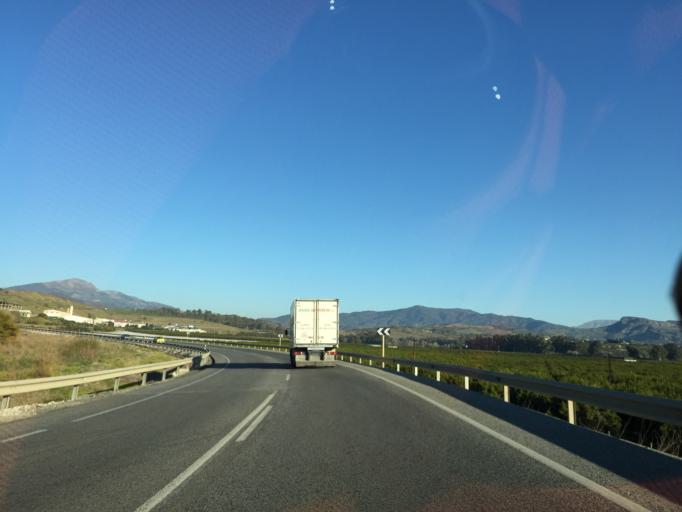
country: ES
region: Andalusia
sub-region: Provincia de Malaga
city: Pizarra
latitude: 36.7538
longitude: -4.7213
